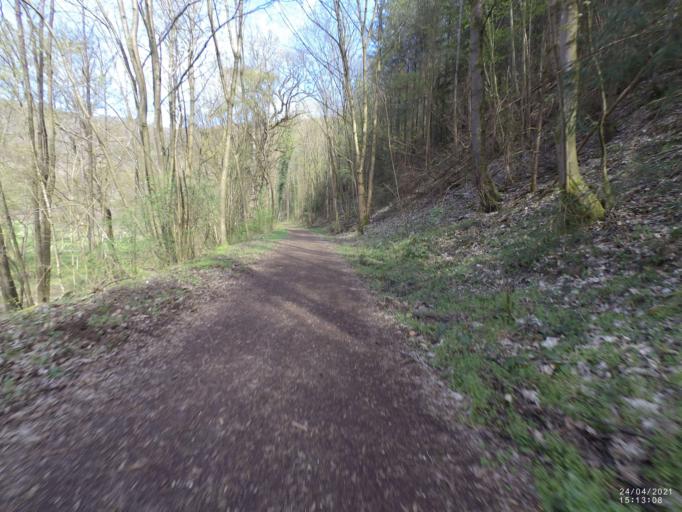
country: DE
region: Rheinland-Pfalz
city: Bendorf
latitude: 50.4461
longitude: 7.5792
